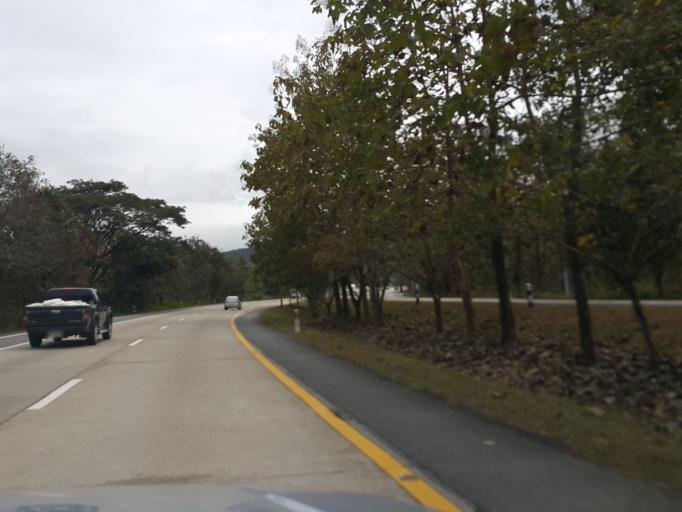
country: TH
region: Lamphun
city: Mae Tha
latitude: 18.4656
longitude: 99.1554
